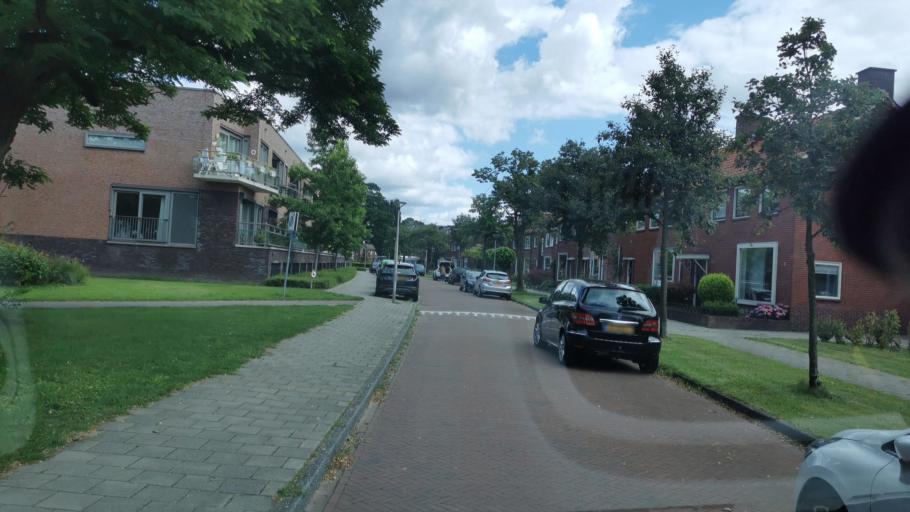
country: NL
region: Overijssel
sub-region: Gemeente Enschede
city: Enschede
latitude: 52.2199
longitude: 6.9195
